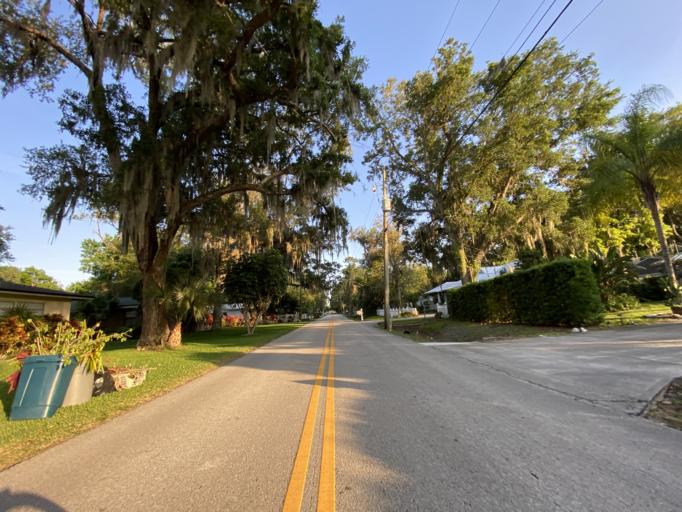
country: US
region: Florida
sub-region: Volusia County
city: Port Orange
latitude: 29.1334
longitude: -81.0060
